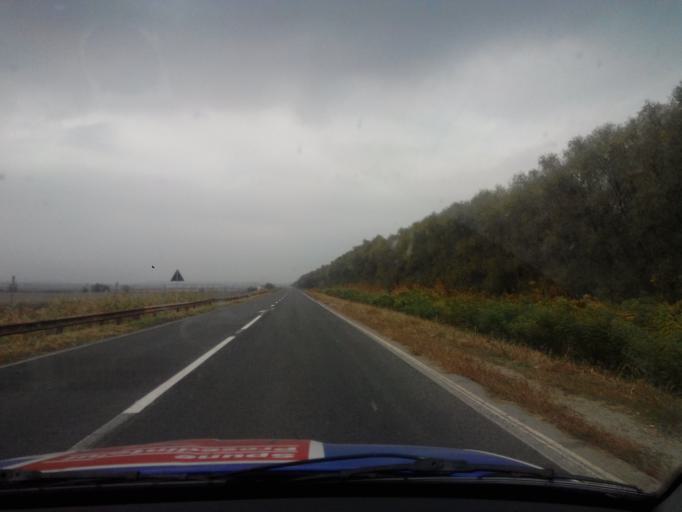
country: RO
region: Braila
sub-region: Comuna Vadeni
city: Vadeni
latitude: 45.3443
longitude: 28.0074
